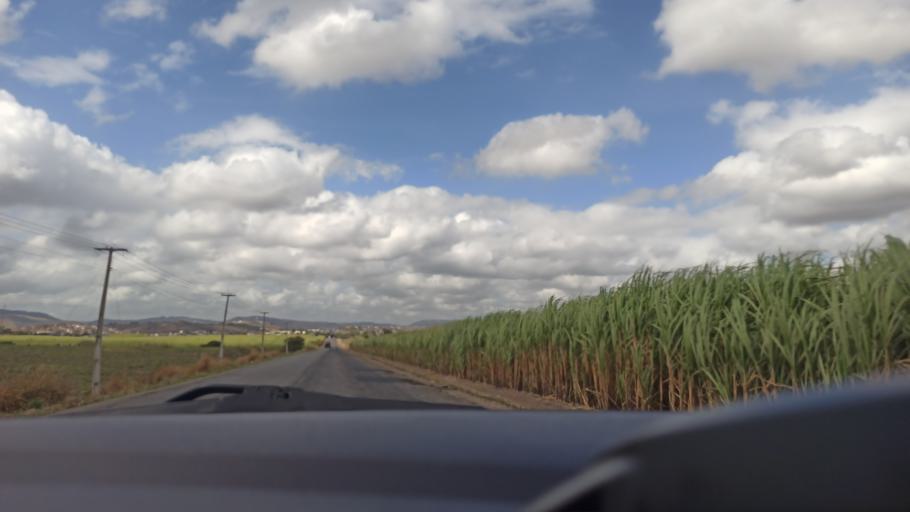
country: BR
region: Pernambuco
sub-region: Timbauba
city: Timbauba
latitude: -7.4844
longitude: -35.2903
